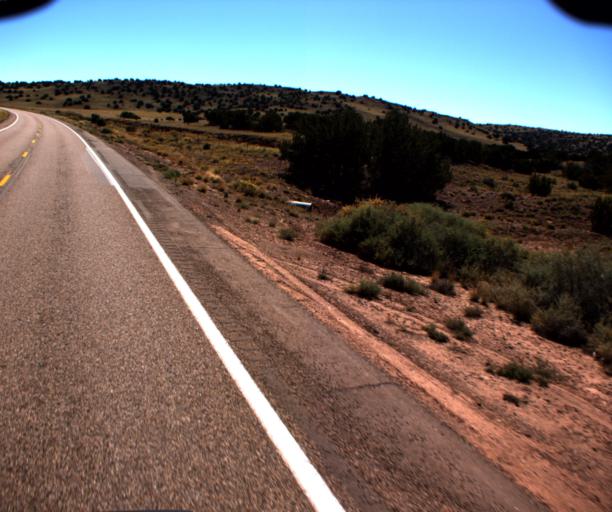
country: US
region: Arizona
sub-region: Apache County
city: Saint Johns
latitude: 34.5721
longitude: -109.5249
